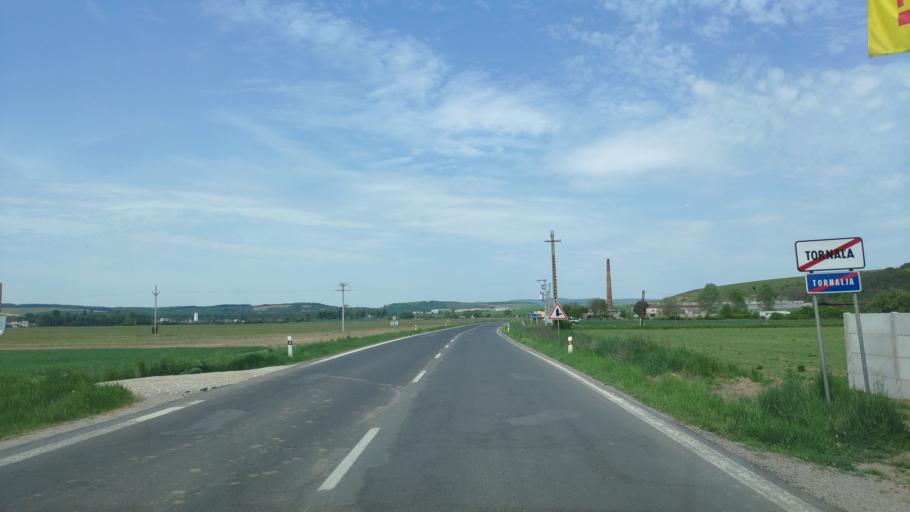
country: HU
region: Borsod-Abauj-Zemplen
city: Putnok
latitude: 48.4247
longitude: 20.3127
